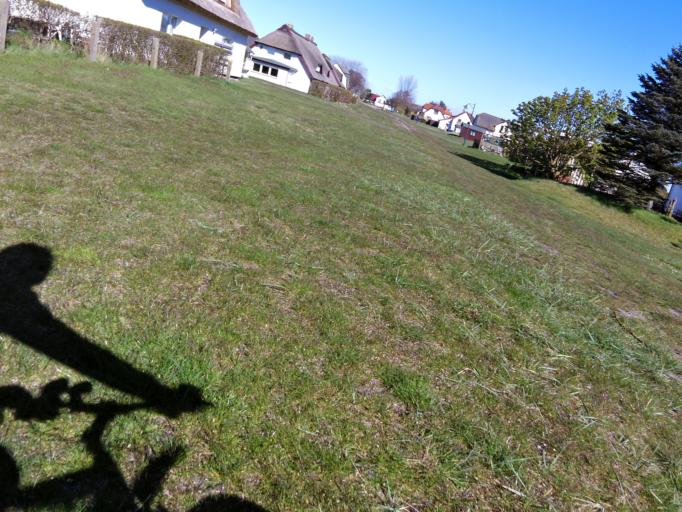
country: DE
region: Mecklenburg-Vorpommern
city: Hiddensee
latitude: 54.5264
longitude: 13.0843
